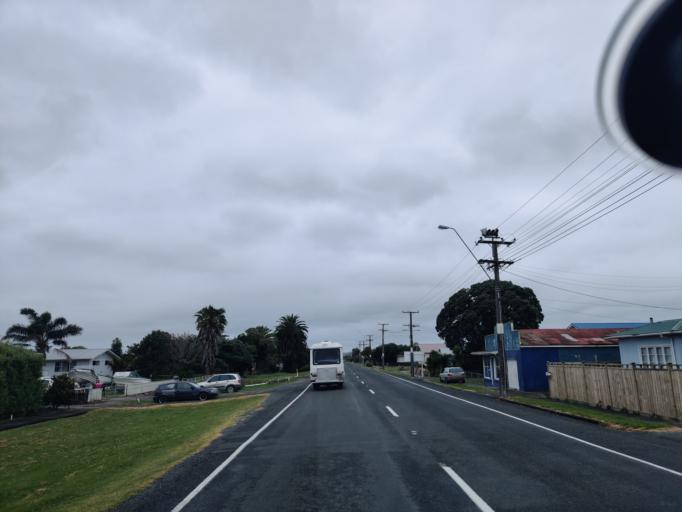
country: NZ
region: Northland
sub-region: Kaipara District
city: Dargaville
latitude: -36.1352
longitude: 174.0258
